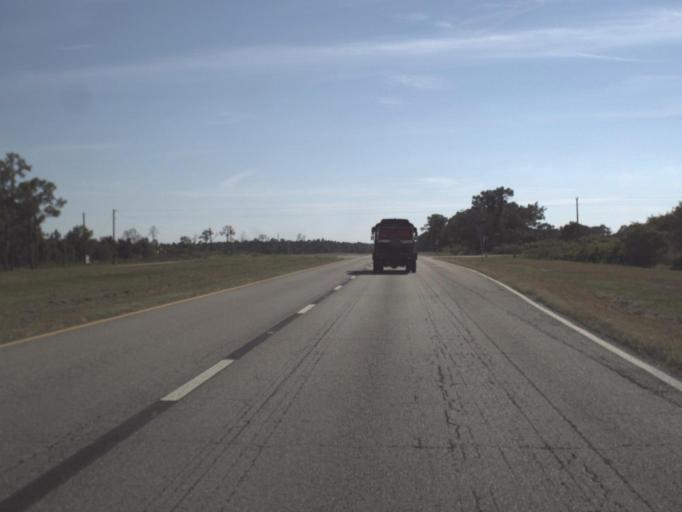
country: US
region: Florida
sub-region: Highlands County
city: Placid Lakes
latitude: 27.0680
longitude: -81.3370
